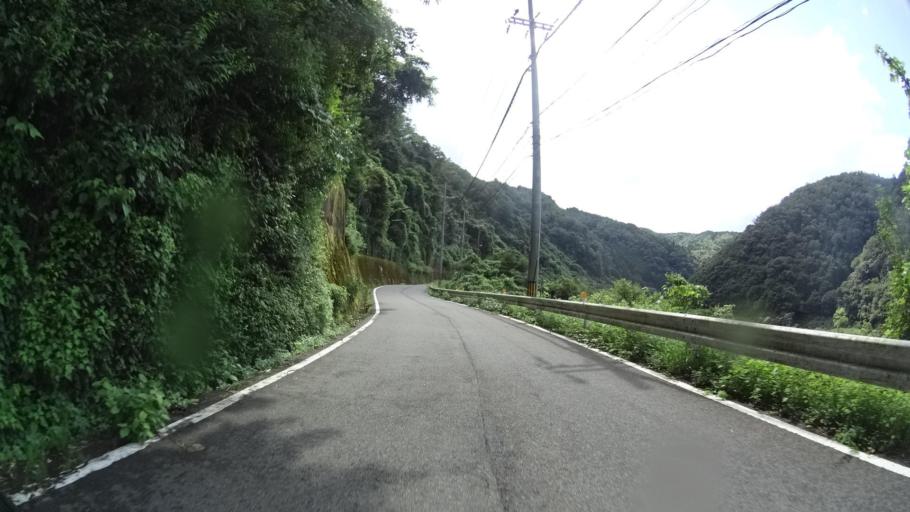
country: JP
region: Mie
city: Ueno-ebisumachi
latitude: 34.7647
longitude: 136.0020
